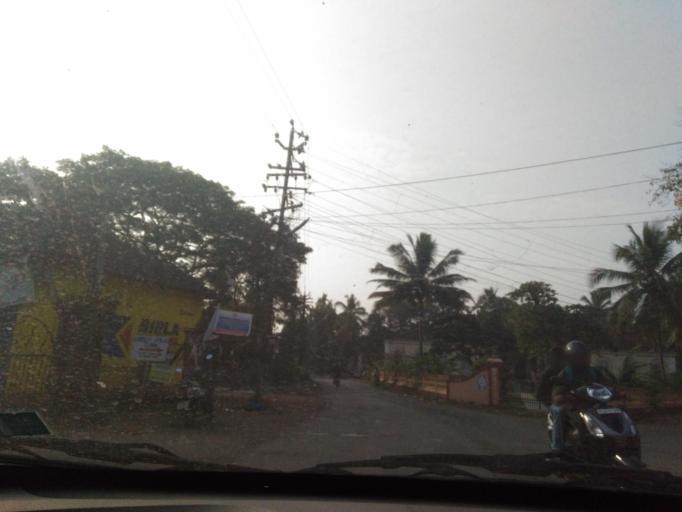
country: IN
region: Goa
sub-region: South Goa
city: Cuncolim
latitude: 15.1802
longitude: 73.9713
